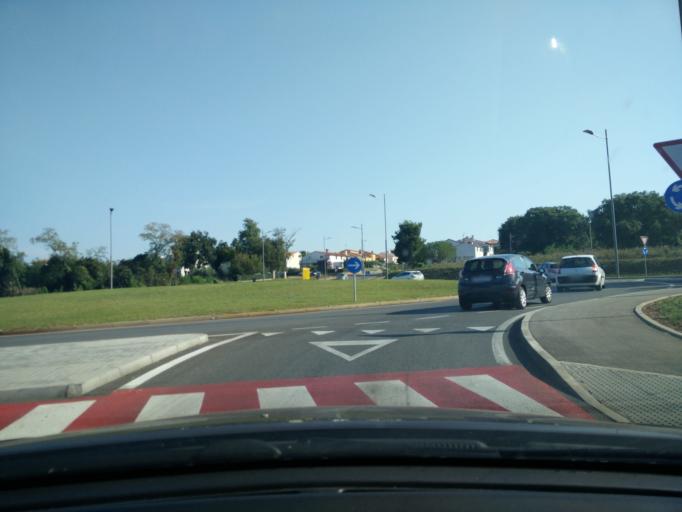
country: HR
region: Istarska
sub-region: Grad Porec
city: Porec
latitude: 45.2441
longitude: 13.6077
